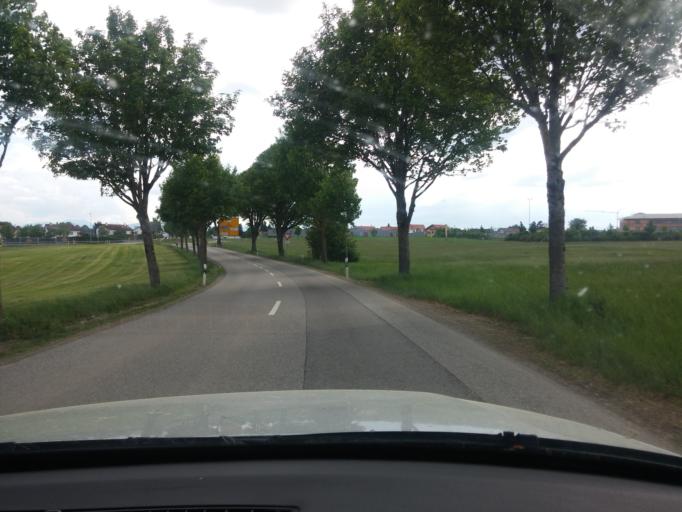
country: DE
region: Bavaria
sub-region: Upper Bavaria
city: Holzkirchen
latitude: 47.8907
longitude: 11.7092
